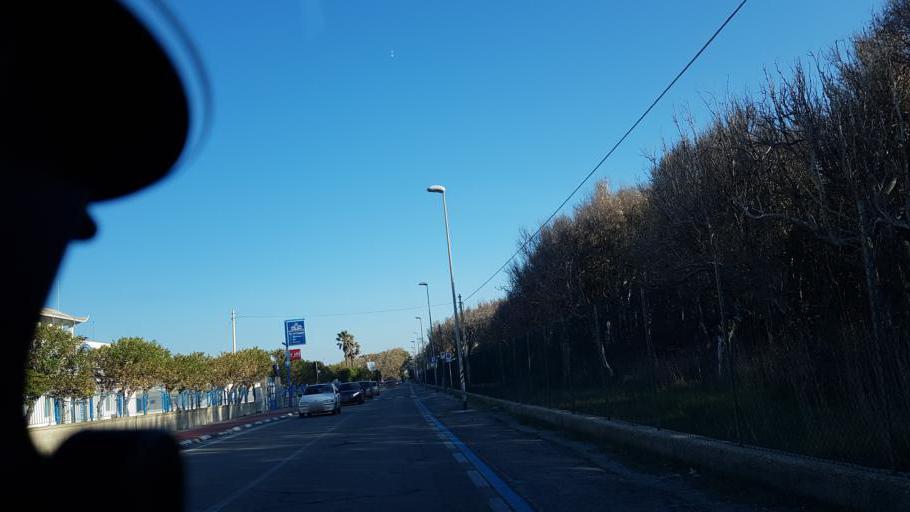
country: IT
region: Apulia
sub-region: Provincia di Lecce
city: Struda
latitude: 40.3792
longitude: 18.3091
